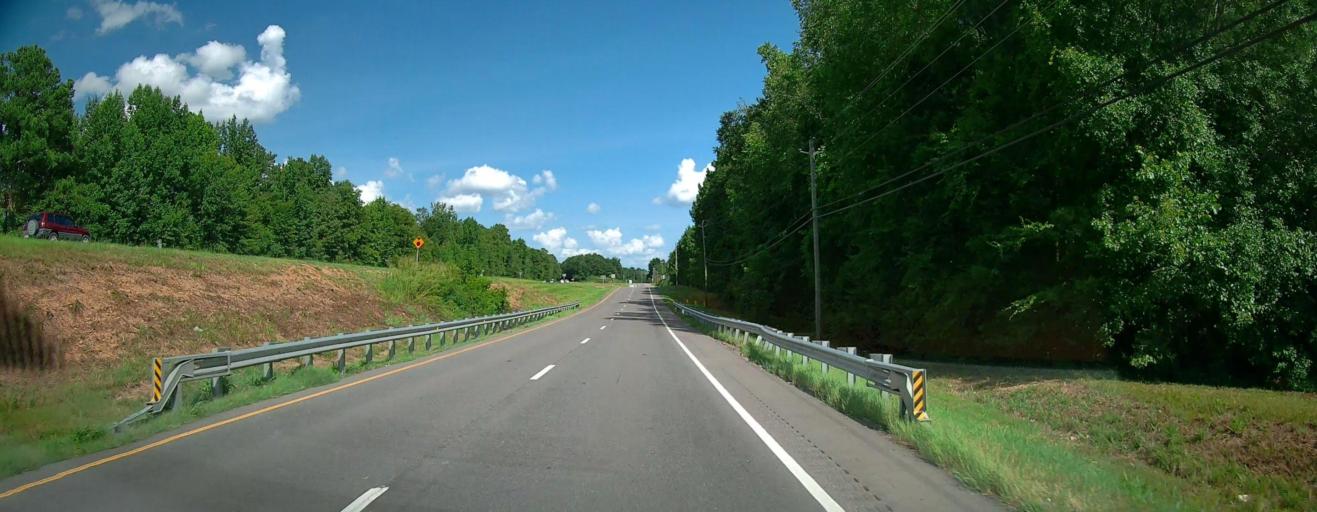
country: US
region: Alabama
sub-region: Tuscaloosa County
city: Northport
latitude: 33.2401
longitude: -87.6616
